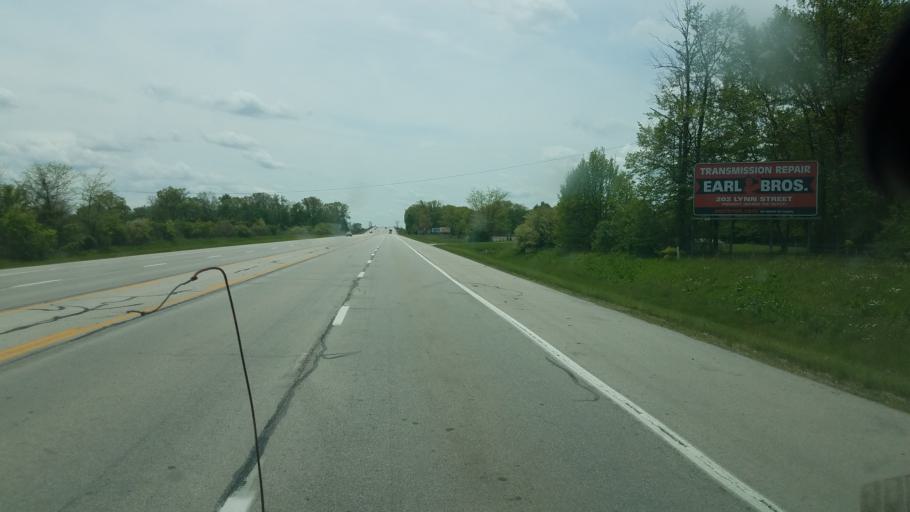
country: US
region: Ohio
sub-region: Sandusky County
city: Fremont
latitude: 41.3925
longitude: -83.1112
